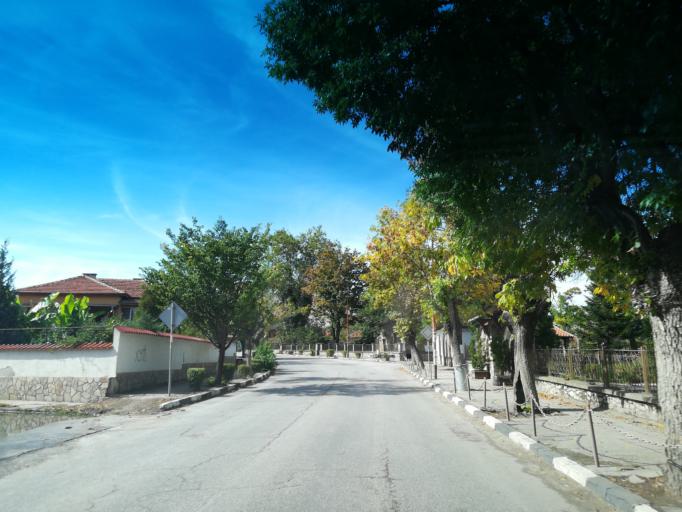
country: BG
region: Plovdiv
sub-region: Obshtina Krichim
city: Krichim
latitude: 42.1046
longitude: 24.4812
